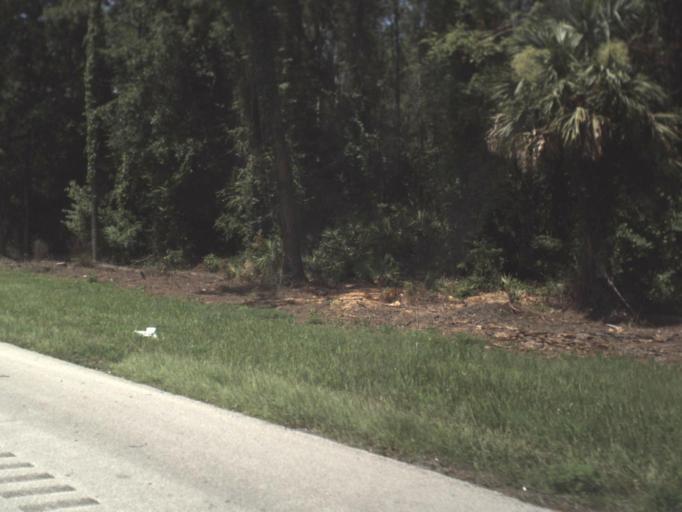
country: US
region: Florida
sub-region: Saint Johns County
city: Saint Augustine
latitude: 29.8884
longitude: -81.4034
